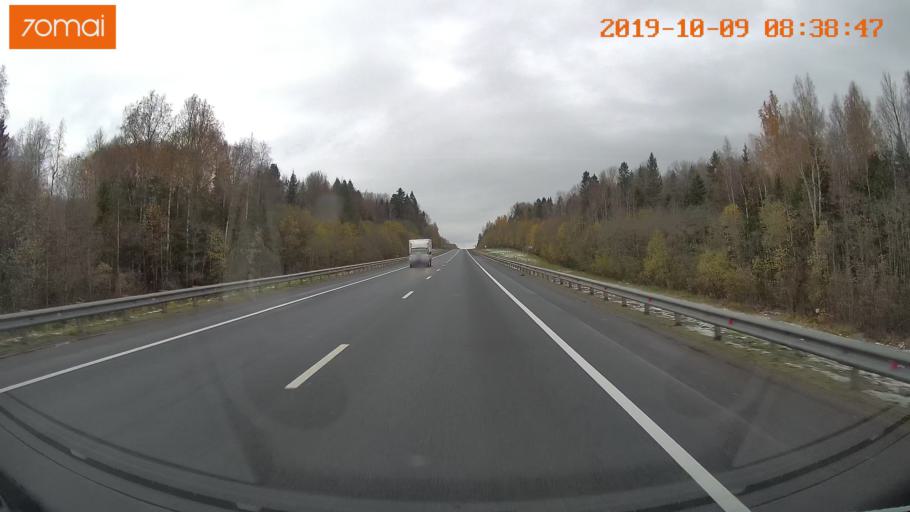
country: RU
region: Vologda
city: Gryazovets
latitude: 58.9616
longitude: 40.1614
